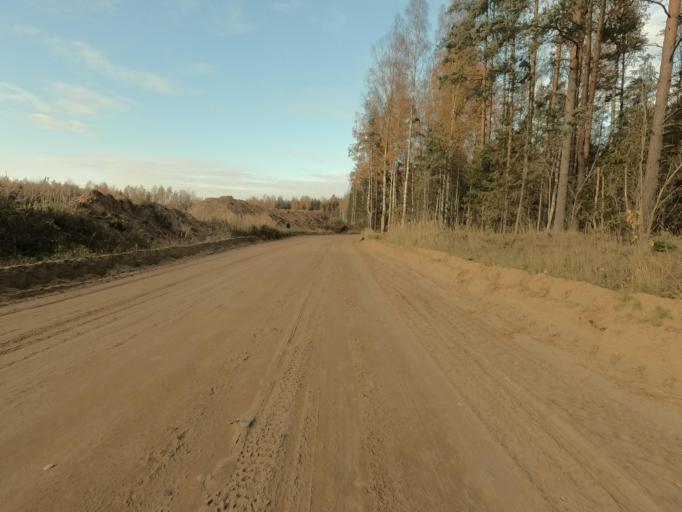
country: RU
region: Leningrad
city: Priladozhskiy
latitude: 59.7368
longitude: 31.3170
